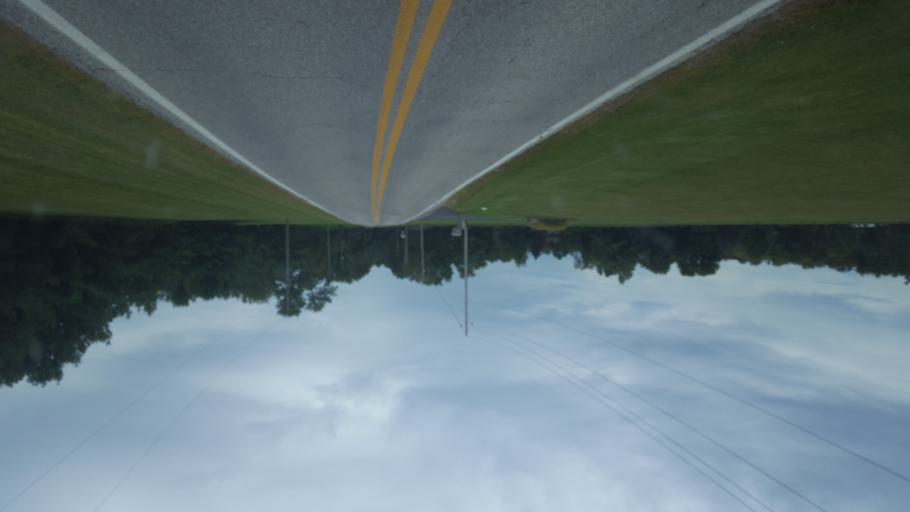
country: US
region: Ohio
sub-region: Delaware County
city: Sunbury
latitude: 40.2547
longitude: -82.8300
